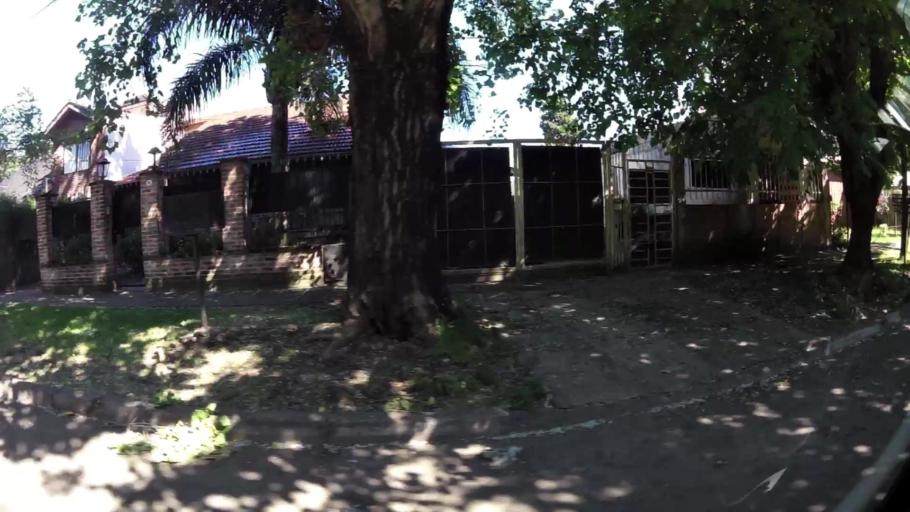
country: AR
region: Buenos Aires
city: Ituzaingo
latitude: -34.6299
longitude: -58.6591
